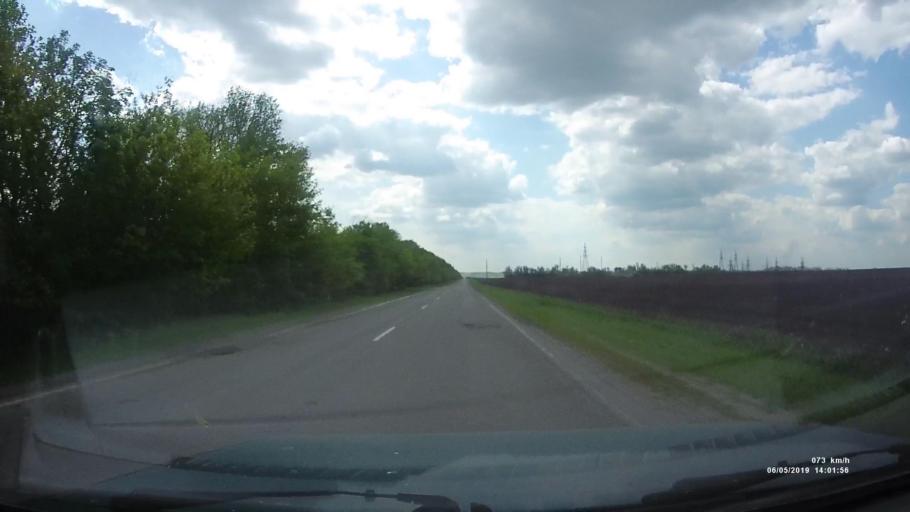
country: RU
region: Rostov
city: Shakhty
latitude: 47.6837
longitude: 40.3715
